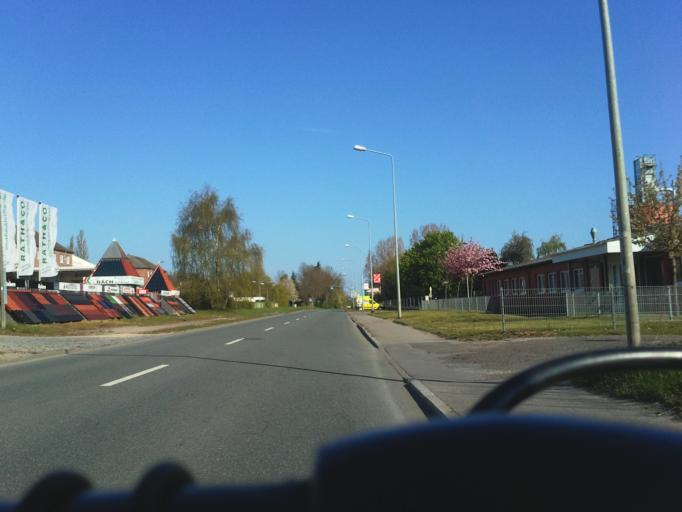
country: DE
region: Mecklenburg-Vorpommern
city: Rostock
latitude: 54.1001
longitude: 12.0952
